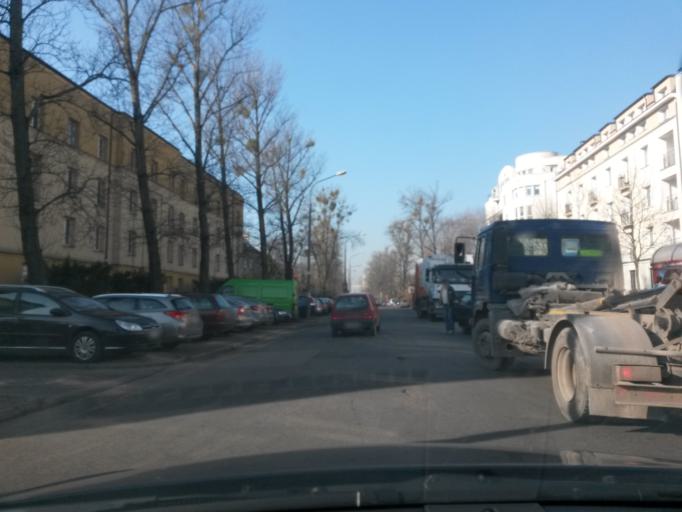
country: PL
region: Masovian Voivodeship
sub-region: Warszawa
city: Mokotow
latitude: 52.1946
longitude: 21.0236
